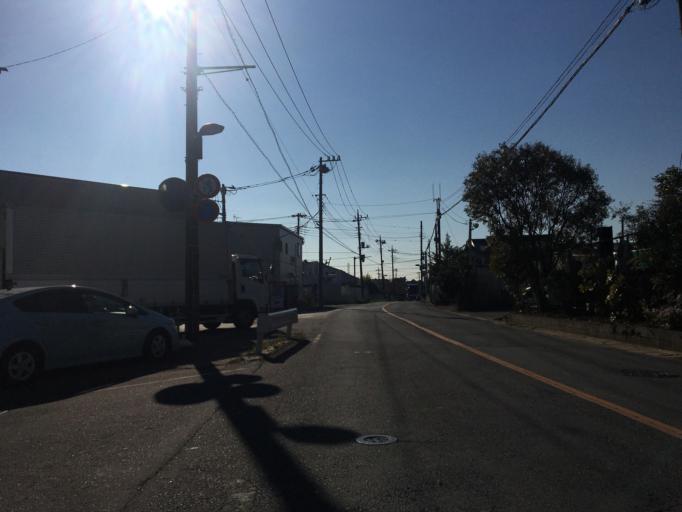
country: JP
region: Saitama
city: Yashio-shi
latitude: 35.8117
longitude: 139.8264
